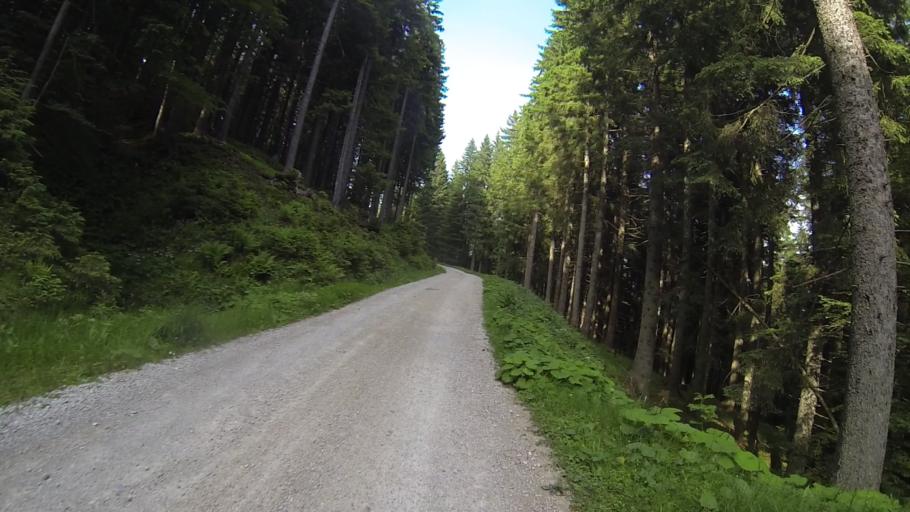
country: DE
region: Bavaria
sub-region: Swabia
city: Nesselwang
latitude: 47.5892
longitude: 10.5066
